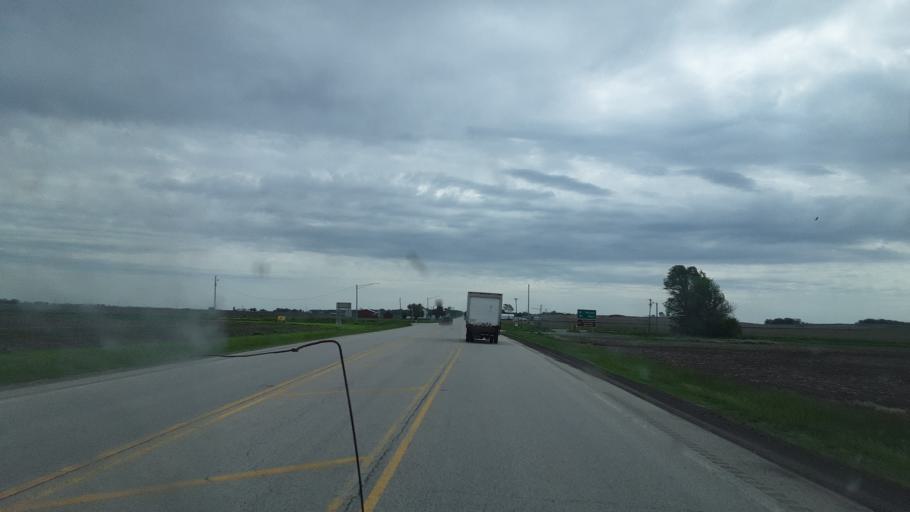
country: US
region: Illinois
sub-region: Mason County
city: Mason City
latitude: 40.3051
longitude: -89.6427
